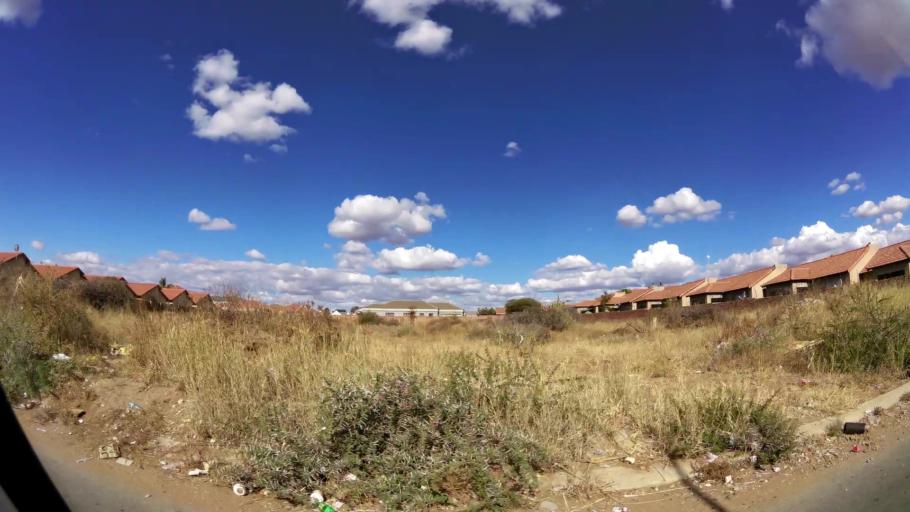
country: ZA
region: Limpopo
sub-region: Capricorn District Municipality
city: Polokwane
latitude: -23.8739
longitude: 29.4847
